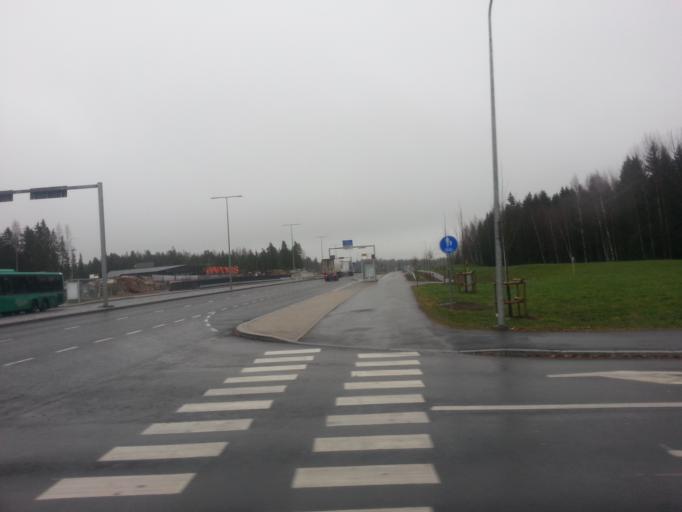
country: FI
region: Uusimaa
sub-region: Helsinki
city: Vantaa
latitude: 60.3022
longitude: 24.9514
